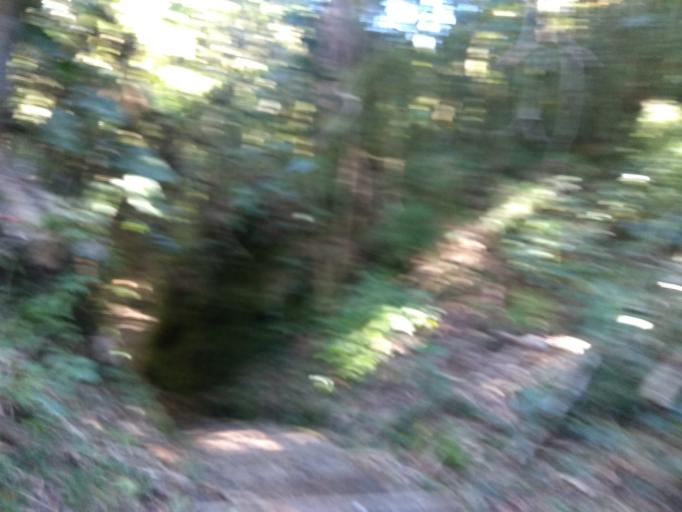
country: CR
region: Heredia
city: Santo Domingo
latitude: 10.1312
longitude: -84.1218
